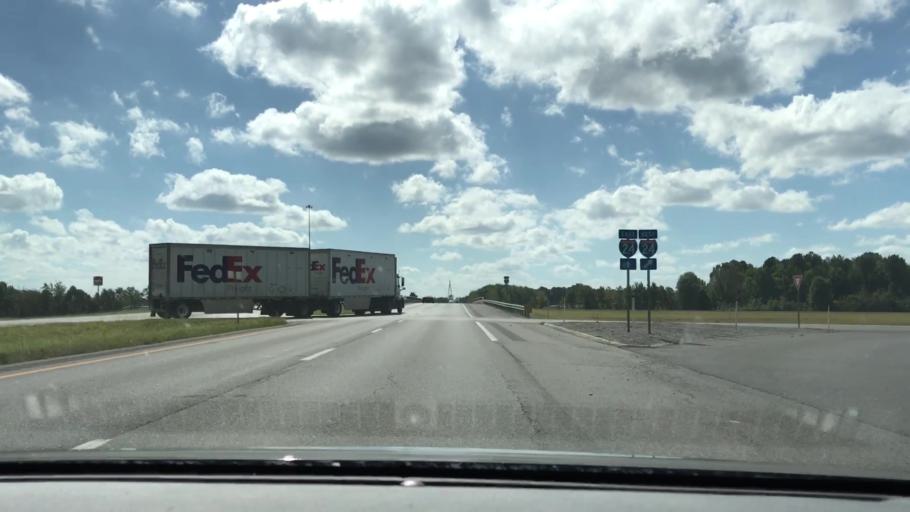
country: US
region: Kentucky
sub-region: McCracken County
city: Reidland
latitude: 36.9963
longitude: -88.5063
